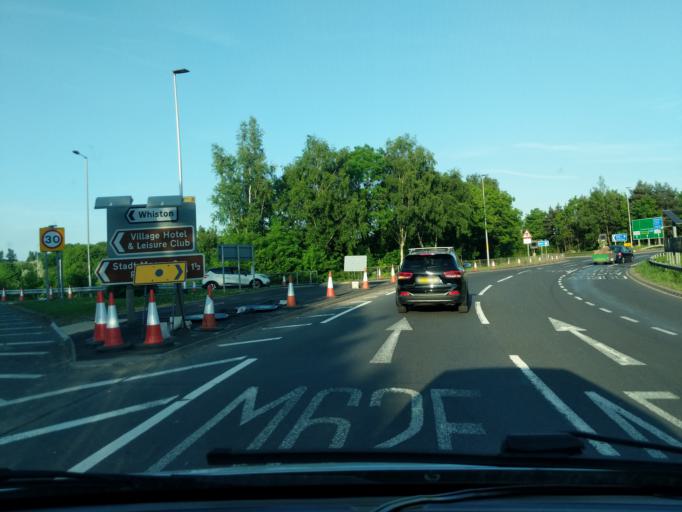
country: GB
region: England
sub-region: Knowsley
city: Whiston
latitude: 53.3998
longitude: -2.8081
